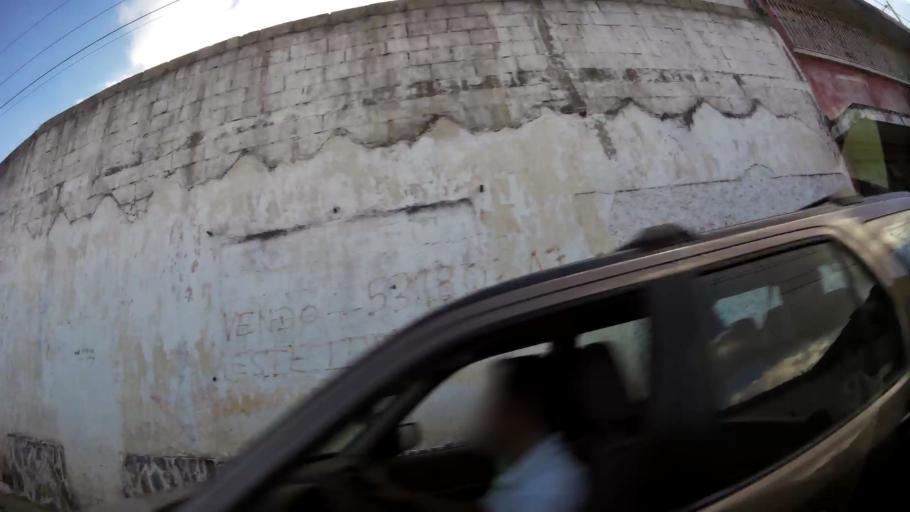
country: GT
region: Guatemala
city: Villa Nueva
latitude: 14.5181
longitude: -90.5851
